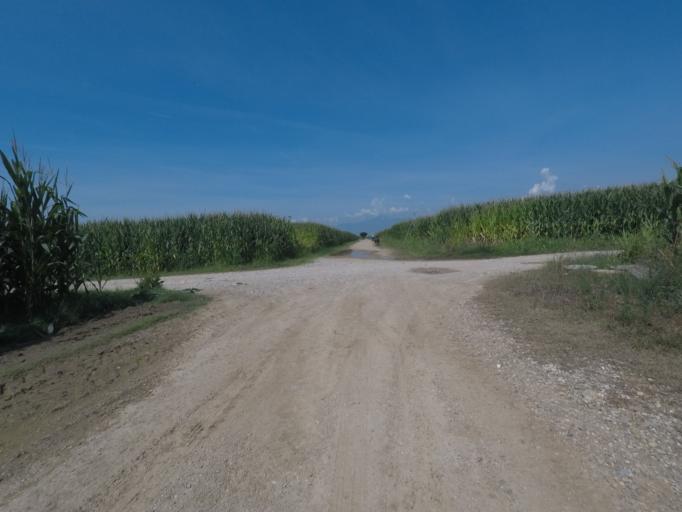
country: IT
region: Friuli Venezia Giulia
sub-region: Provincia di Udine
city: Flaibano
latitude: 46.0821
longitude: 12.9746
